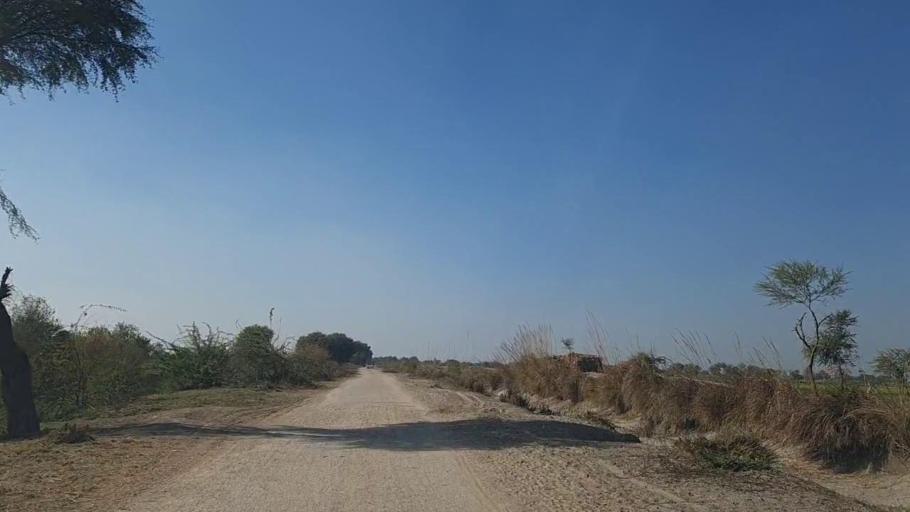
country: PK
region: Sindh
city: Shahpur Chakar
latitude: 26.2118
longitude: 68.6147
